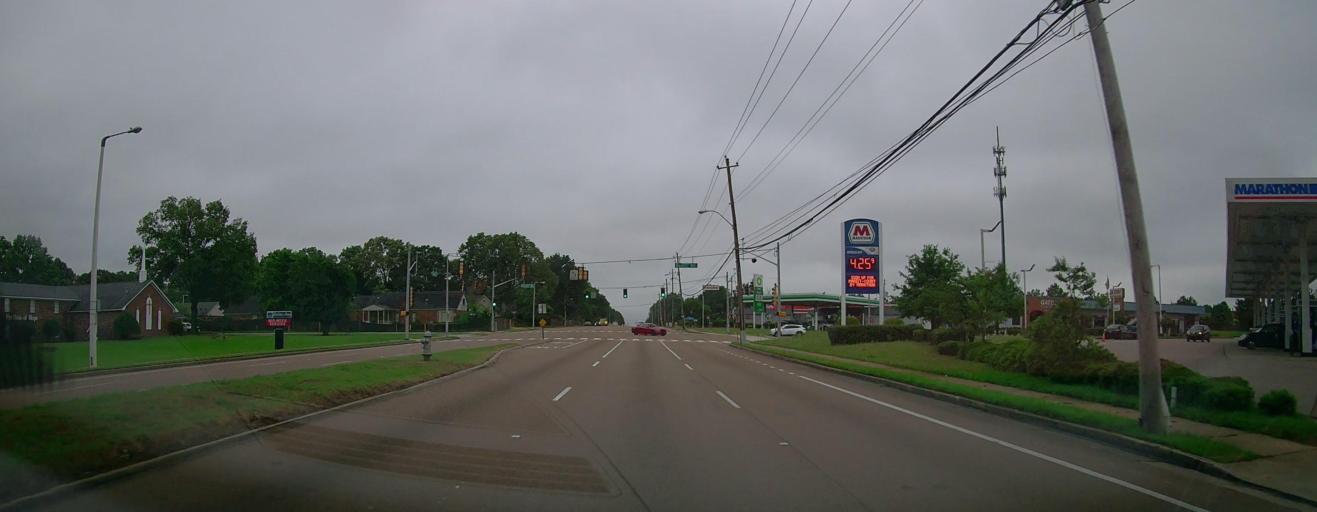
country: US
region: Tennessee
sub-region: Shelby County
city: Germantown
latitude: 35.0359
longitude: -89.8314
